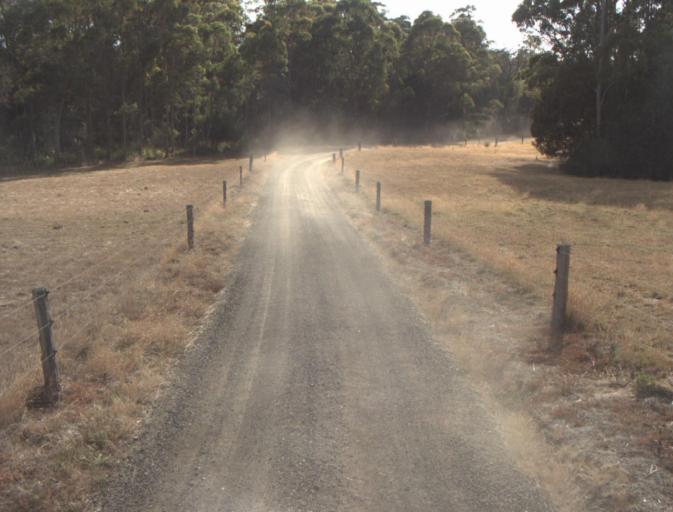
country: AU
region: Tasmania
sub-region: Dorset
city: Bridport
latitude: -41.1255
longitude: 147.2065
